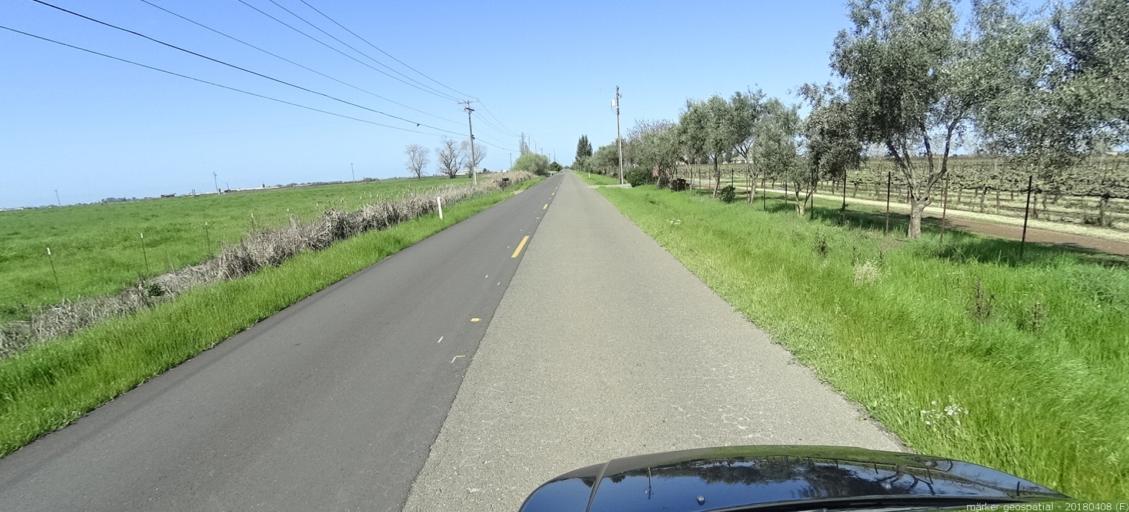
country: US
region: California
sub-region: Sacramento County
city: Elk Grove
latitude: 38.3508
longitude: -121.3776
